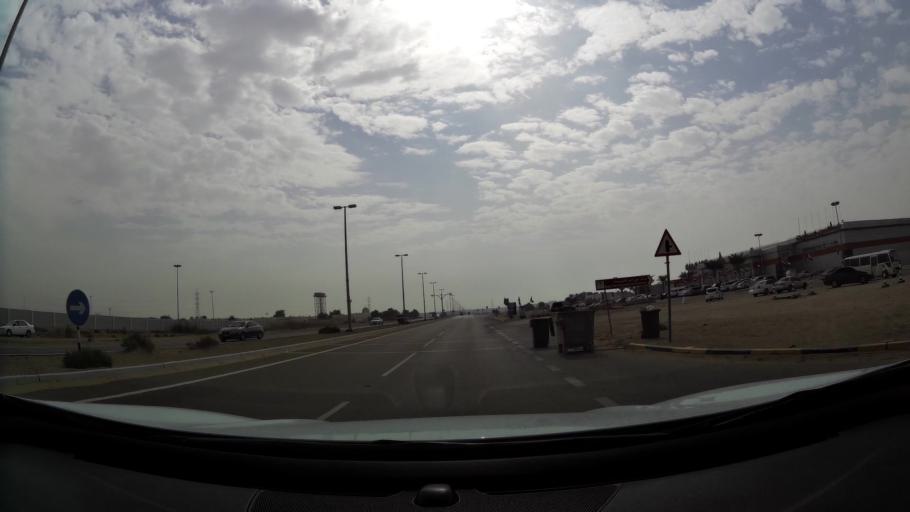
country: AE
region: Abu Dhabi
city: Abu Dhabi
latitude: 24.2879
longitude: 54.6636
